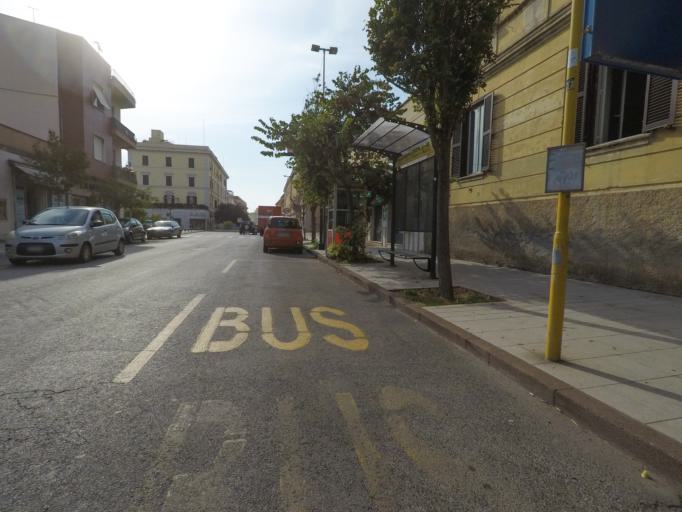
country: IT
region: Latium
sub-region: Citta metropolitana di Roma Capitale
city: Civitavecchia
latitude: 42.0928
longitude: 11.7961
